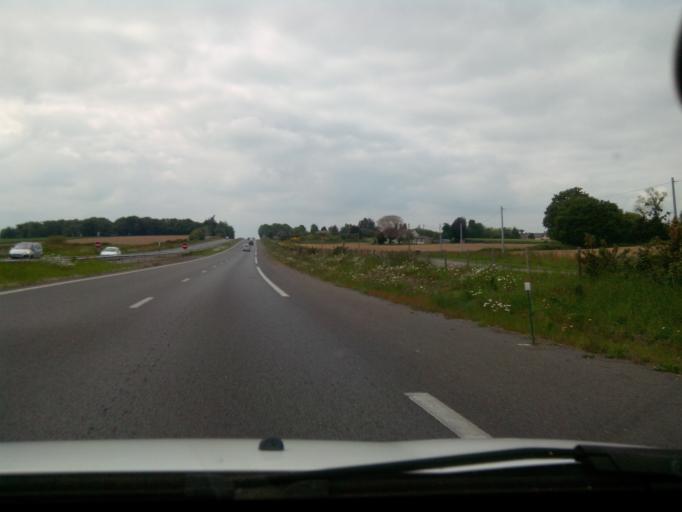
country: FR
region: Brittany
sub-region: Departement d'Ille-et-Vilaine
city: Montauban-de-Bretagne
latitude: 48.2109
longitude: -2.0820
